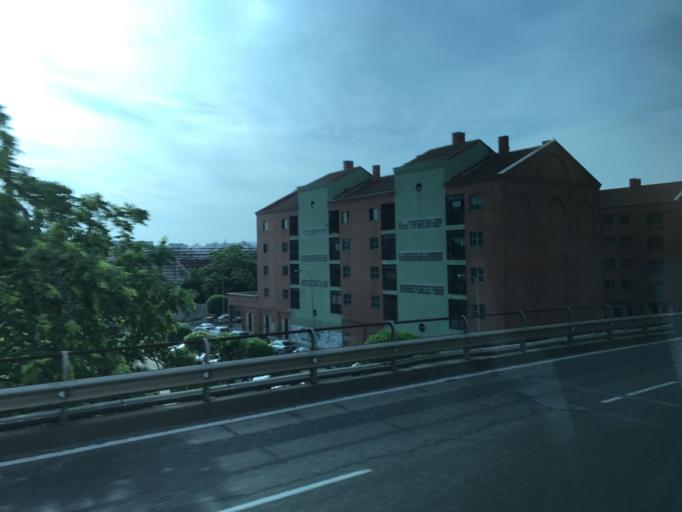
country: ES
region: Castille and Leon
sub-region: Provincia de Valladolid
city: Valladolid
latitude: 41.6405
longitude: -4.7311
